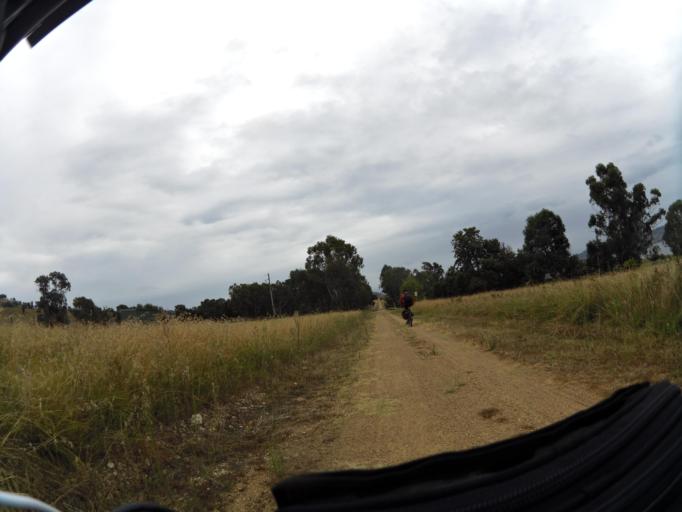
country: AU
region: New South Wales
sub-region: Albury Municipality
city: East Albury
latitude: -36.2107
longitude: 147.0546
